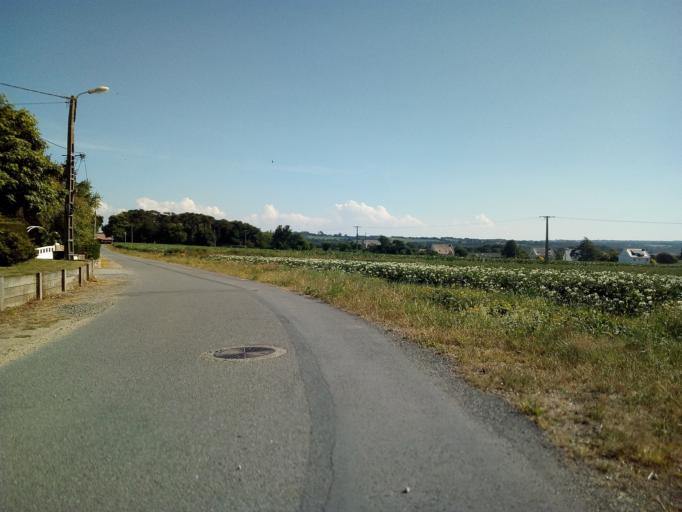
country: FR
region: Brittany
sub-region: Departement du Finistere
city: Landivisiau
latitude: 48.5111
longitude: -4.0913
